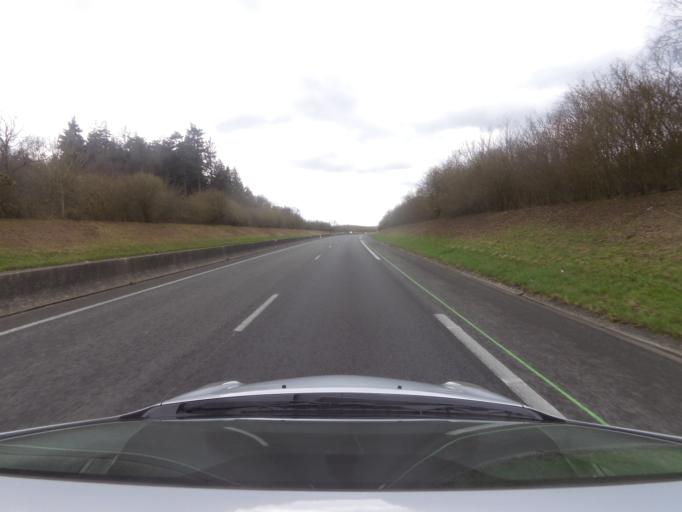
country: FR
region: Nord-Pas-de-Calais
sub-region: Departement du Pas-de-Calais
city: Saint-Josse
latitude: 50.4631
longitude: 1.7026
